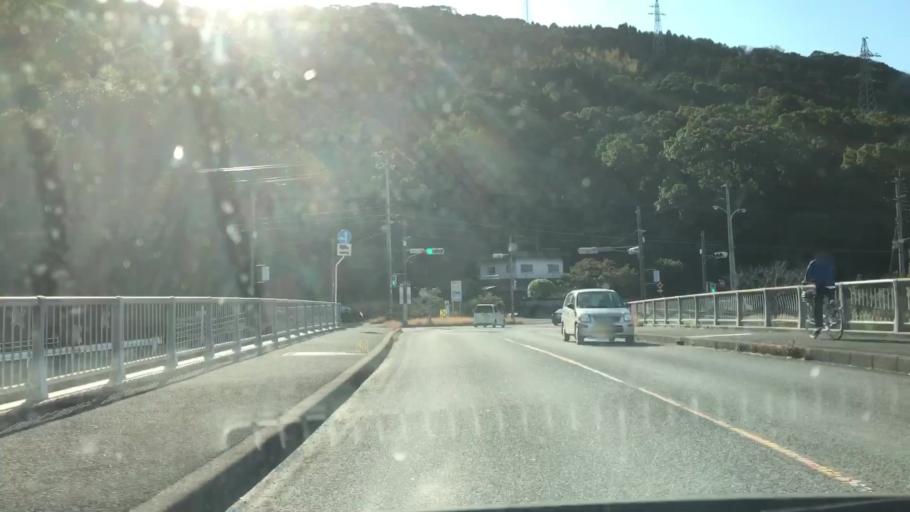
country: JP
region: Kagoshima
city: Satsumasendai
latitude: 31.8144
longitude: 130.2982
